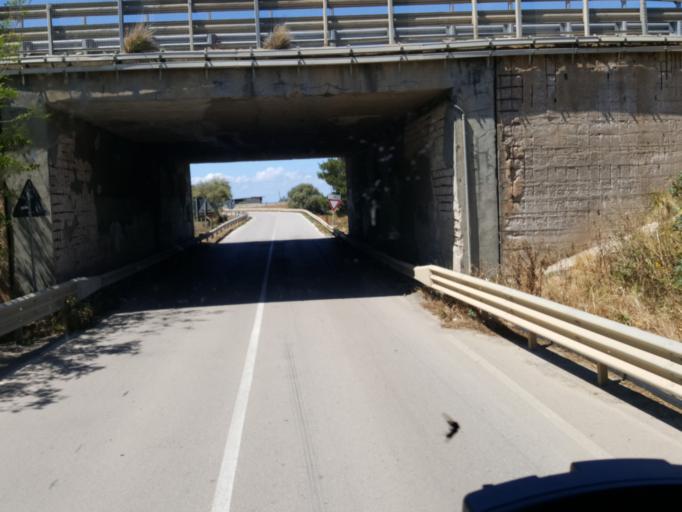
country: IT
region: Sicily
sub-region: Palermo
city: Cerda
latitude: 37.9744
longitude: 13.8083
